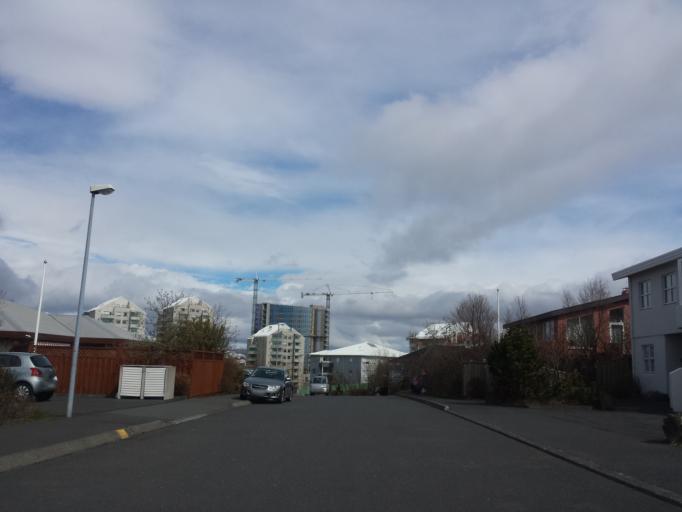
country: IS
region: Capital Region
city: Kopavogur
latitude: 64.1007
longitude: -21.8949
